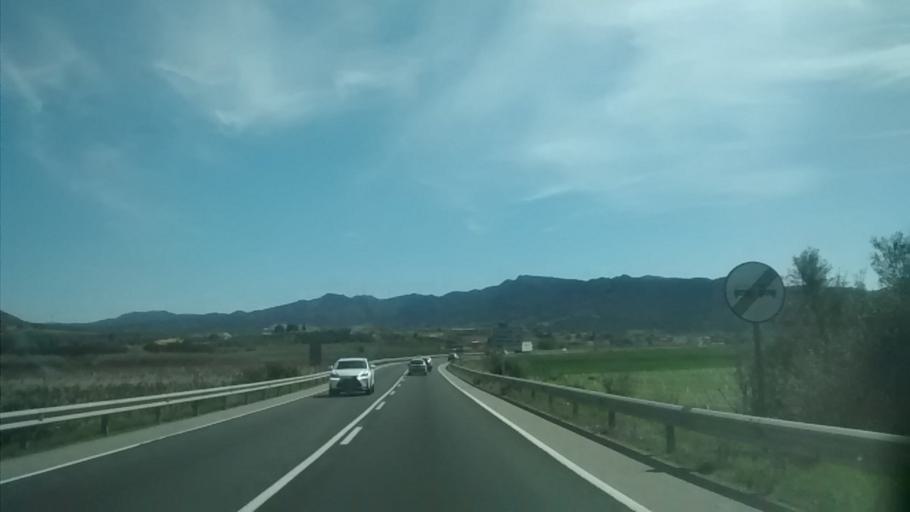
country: ES
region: Catalonia
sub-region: Provincia de Tarragona
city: Asco
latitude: 41.1874
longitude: 0.5730
